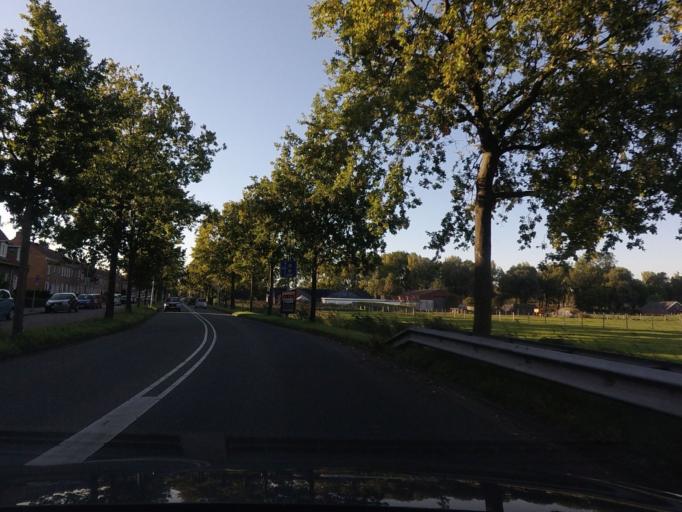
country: NL
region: North Holland
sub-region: Gemeente Bloemendaal
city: Bloemendaal
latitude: 52.4186
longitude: 4.6593
